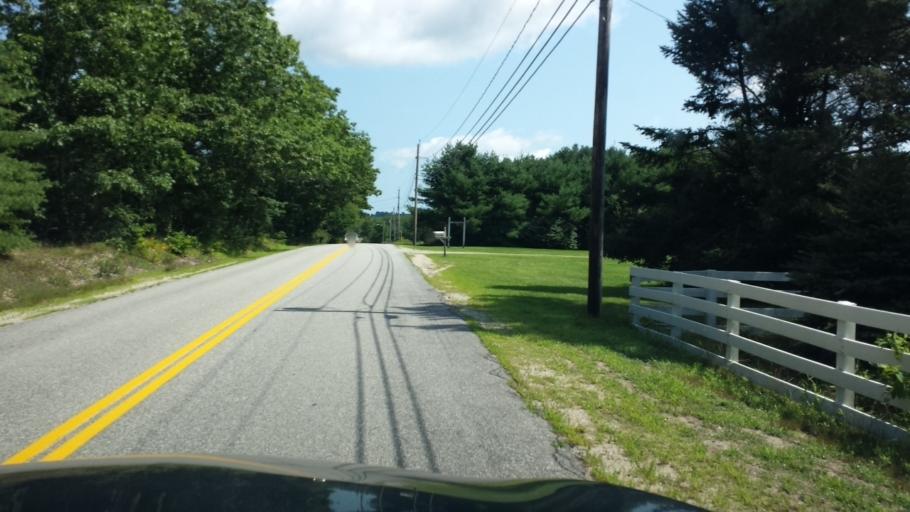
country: US
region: Maine
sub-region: York County
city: West Kennebunk
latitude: 43.4294
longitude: -70.5569
